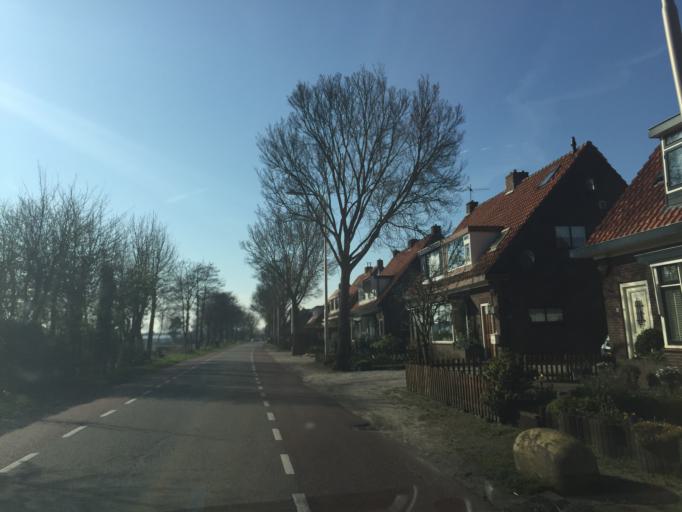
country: NL
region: South Holland
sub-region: Gemeente Hillegom
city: Hillegom
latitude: 52.3126
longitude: 4.5723
